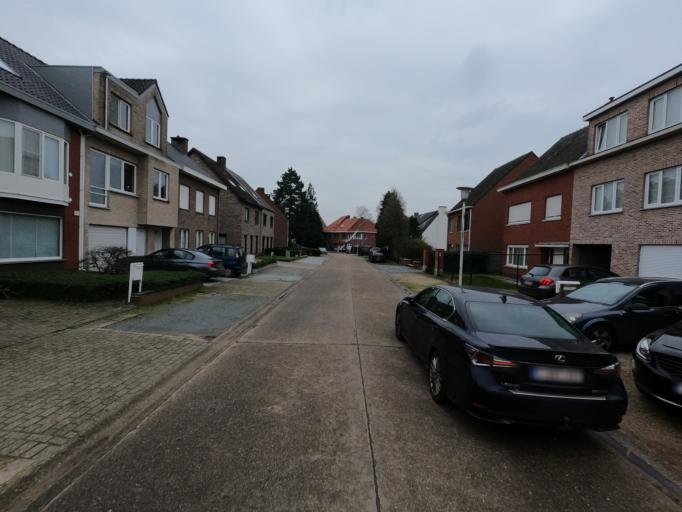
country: BE
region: Flanders
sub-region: Provincie Antwerpen
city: Schilde
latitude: 51.2600
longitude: 4.5513
